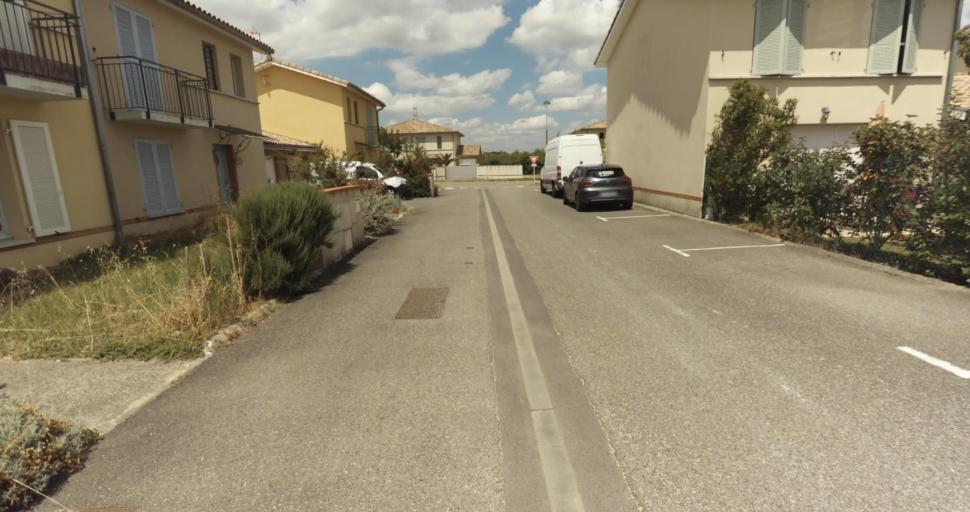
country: FR
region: Midi-Pyrenees
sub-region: Departement de la Haute-Garonne
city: Fontenilles
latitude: 43.5564
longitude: 1.1707
